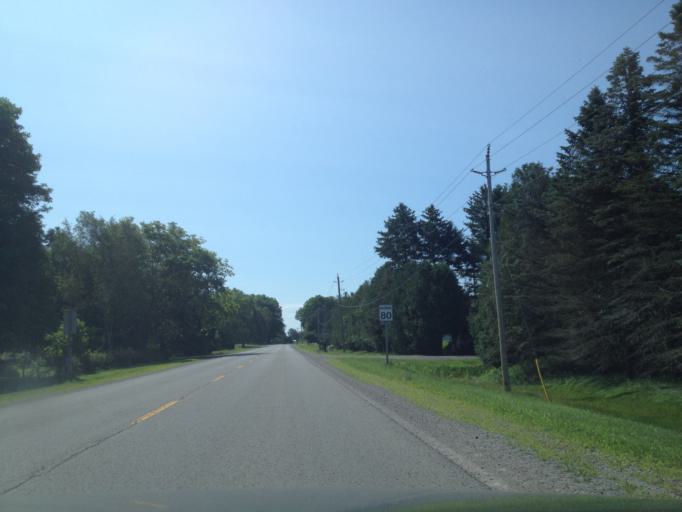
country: CA
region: Ontario
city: Norfolk County
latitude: 42.7945
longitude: -80.4116
